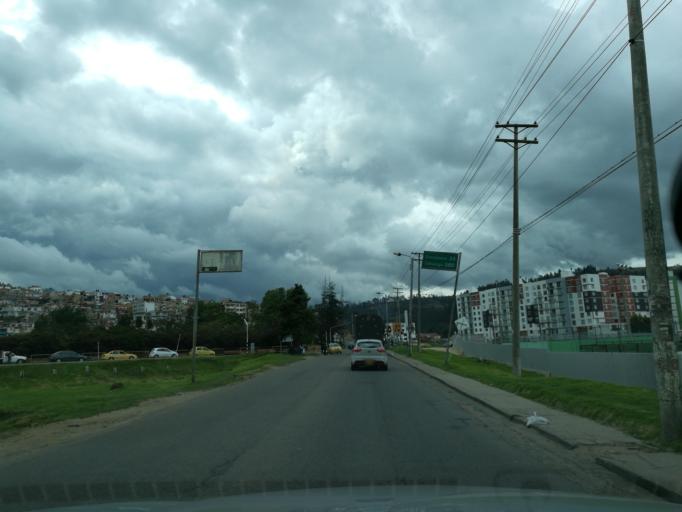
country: CO
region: Boyaca
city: Tunja
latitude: 5.5470
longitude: -73.3588
